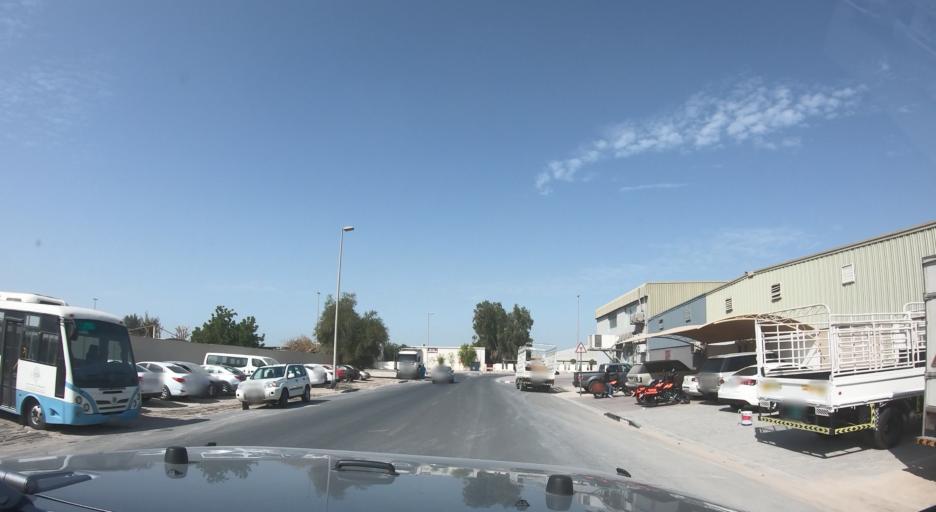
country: AE
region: Dubai
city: Dubai
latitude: 25.1497
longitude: 55.2307
